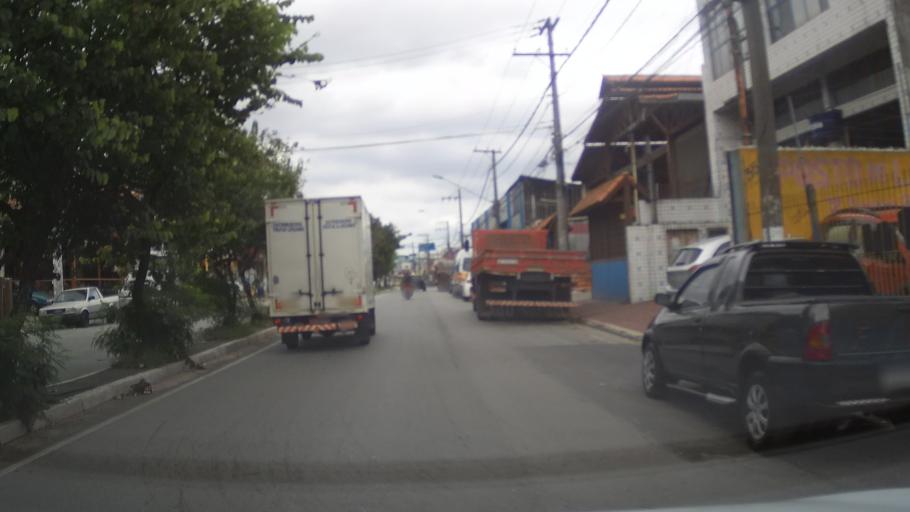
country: BR
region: Sao Paulo
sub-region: Itaquaquecetuba
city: Itaquaquecetuba
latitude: -23.4279
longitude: -46.4338
